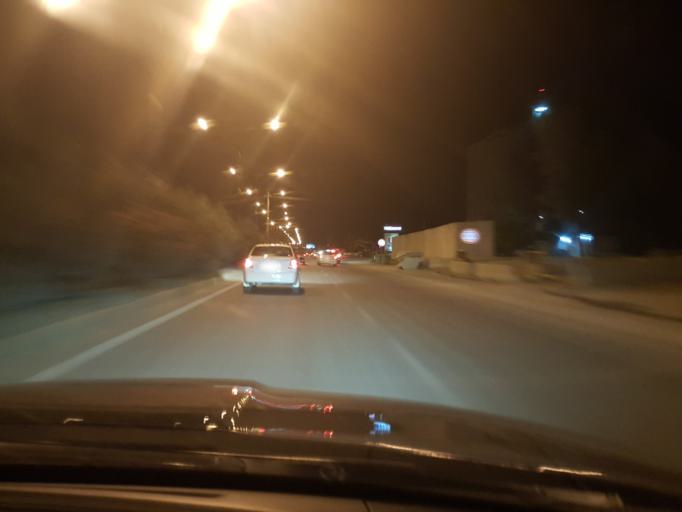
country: IQ
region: Arbil
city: Erbil
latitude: 36.2591
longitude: 44.0857
